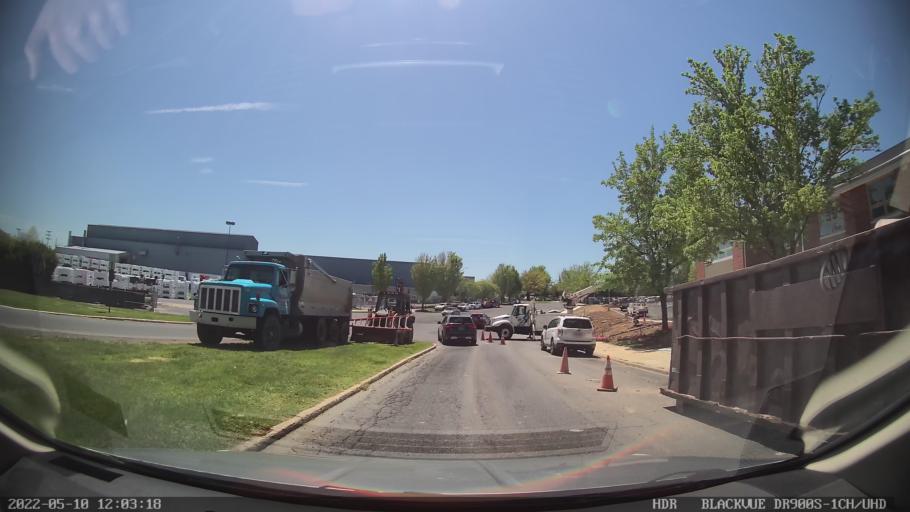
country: US
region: Pennsylvania
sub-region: Berks County
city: Kenhorst
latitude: 40.3212
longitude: -75.9427
